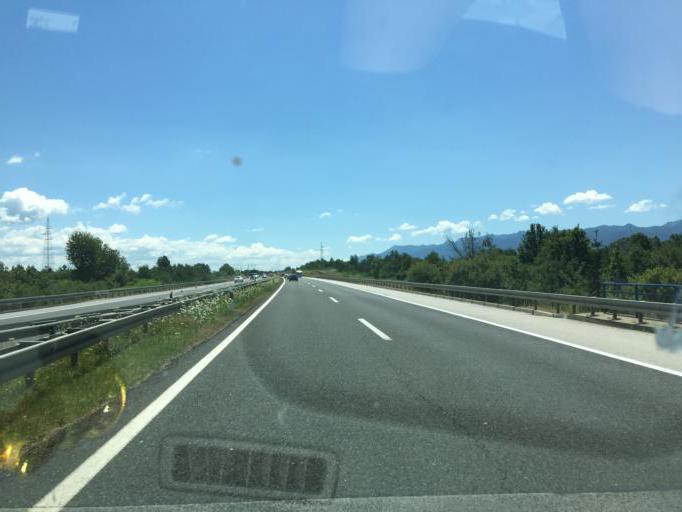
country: HR
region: Licko-Senjska
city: Gospic
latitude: 44.5357
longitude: 15.4423
